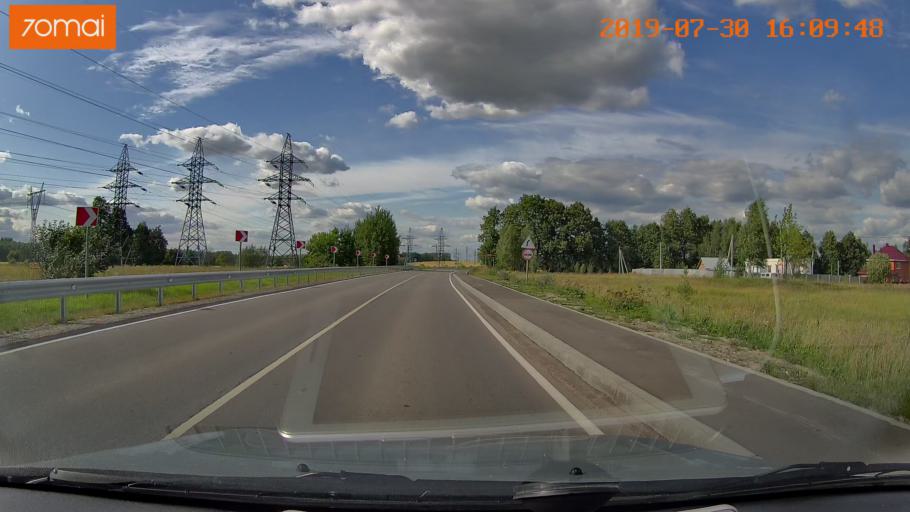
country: RU
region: Moskovskaya
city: Peski
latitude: 55.2563
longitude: 38.7163
